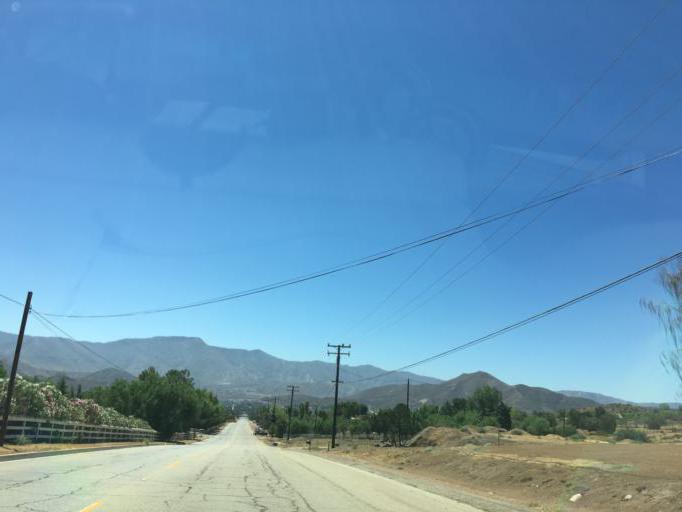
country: US
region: California
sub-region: Los Angeles County
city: Acton
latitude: 34.5030
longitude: -118.1984
